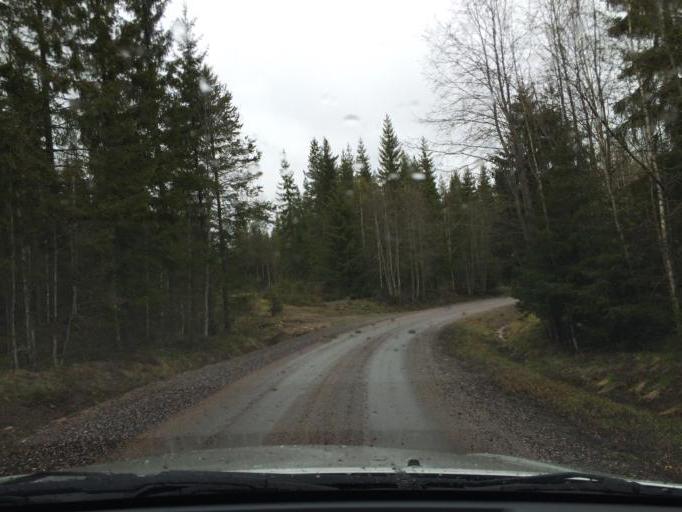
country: SE
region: Dalarna
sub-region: Ludvika Kommun
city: Abborrberget
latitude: 60.0233
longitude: 14.6046
